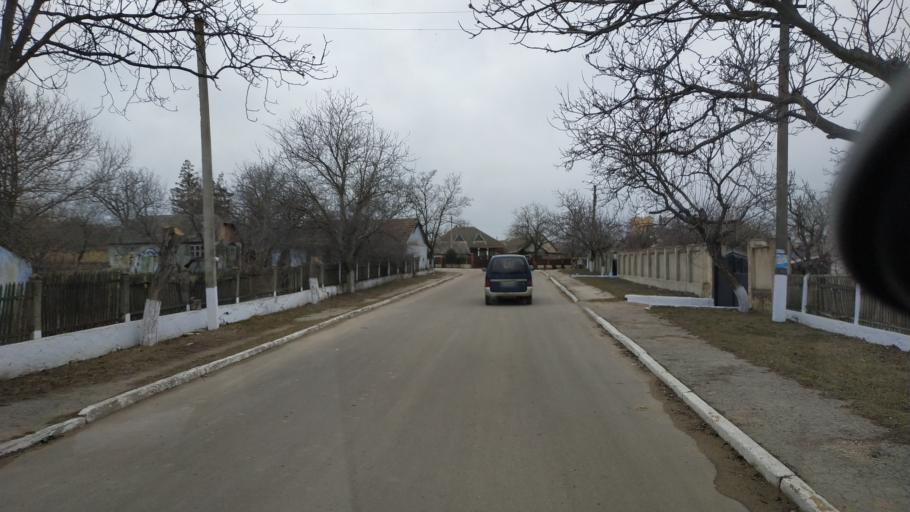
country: MD
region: Telenesti
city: Cocieri
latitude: 47.2580
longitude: 29.0607
